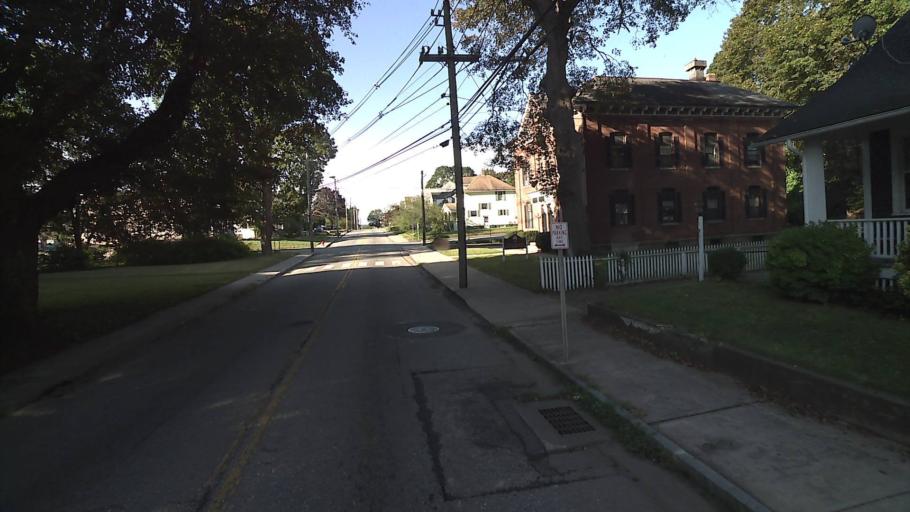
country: US
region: Connecticut
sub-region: New London County
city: Norwich
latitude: 41.5155
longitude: -72.0808
